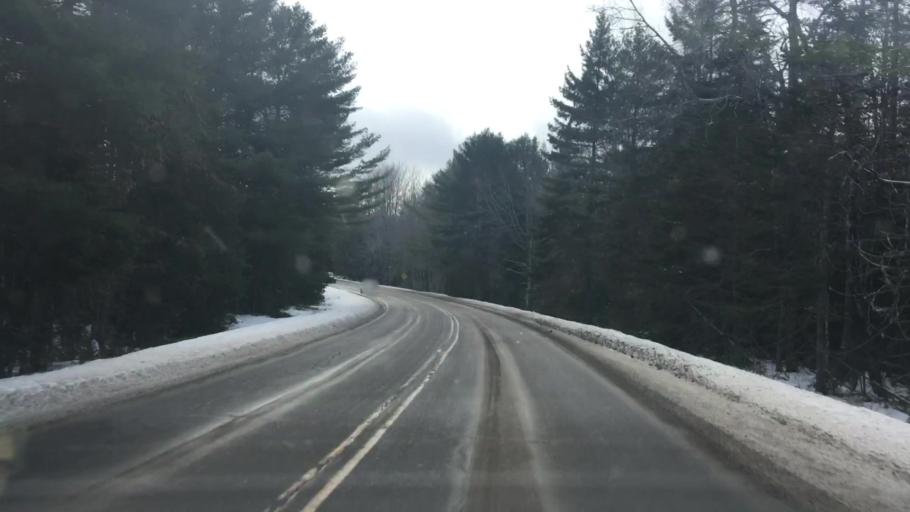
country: US
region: Maine
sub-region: Washington County
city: Calais
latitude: 45.0463
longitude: -67.3276
